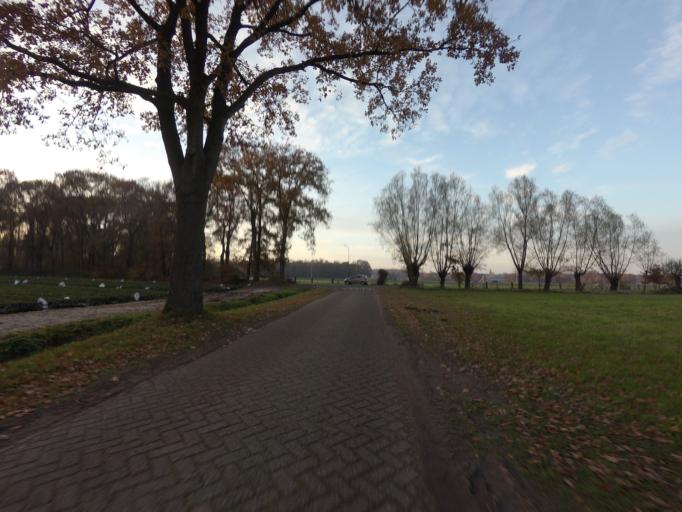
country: NL
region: North Brabant
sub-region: Gemeente Breda
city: Breda
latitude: 51.5304
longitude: 4.7843
